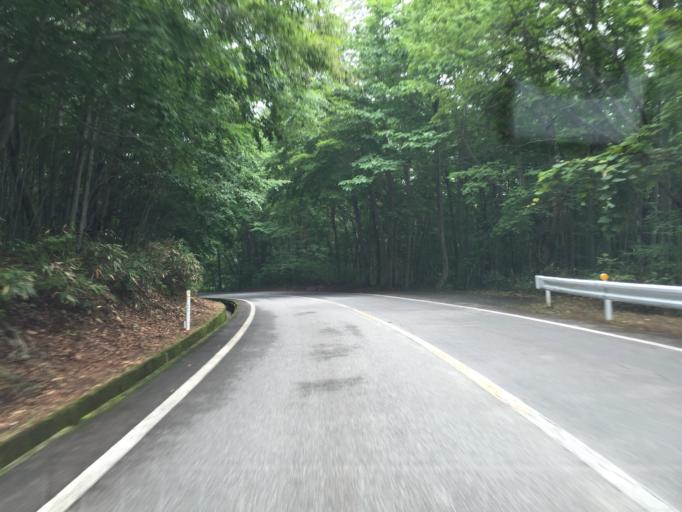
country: JP
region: Fukushima
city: Inawashiro
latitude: 37.6725
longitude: 140.1413
